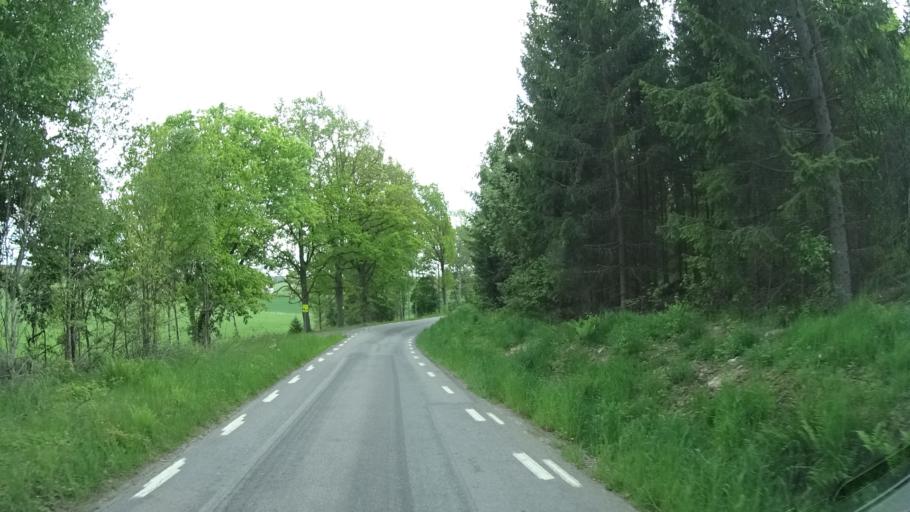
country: SE
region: OEstergoetland
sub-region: Finspangs Kommun
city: Finspang
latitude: 58.5962
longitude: 15.7739
